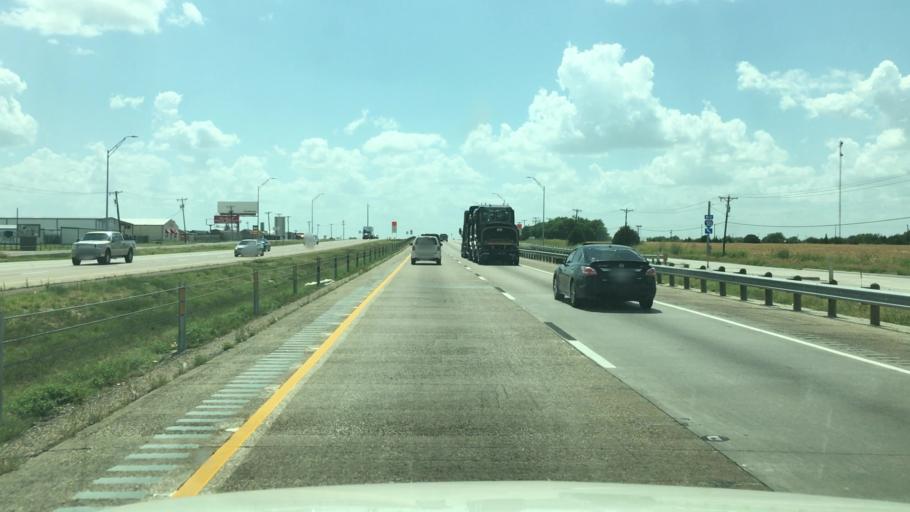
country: US
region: Texas
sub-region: Rockwall County
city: Fate
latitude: 32.9260
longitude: -96.3957
